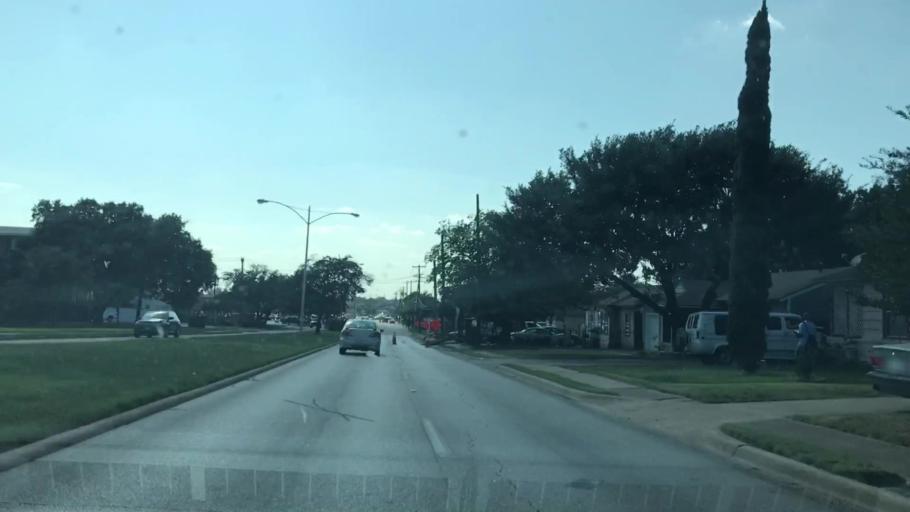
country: US
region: Texas
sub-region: Dallas County
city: Garland
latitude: 32.8349
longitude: -96.6689
